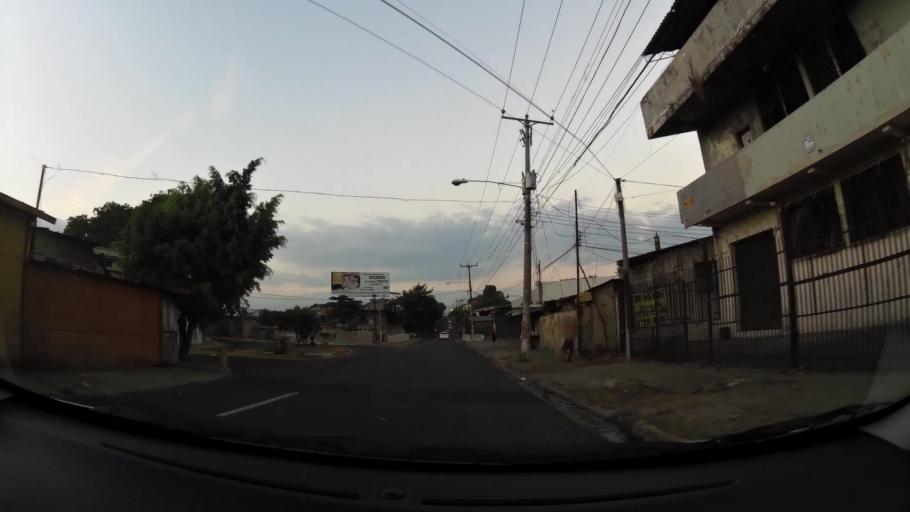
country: SV
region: San Salvador
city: San Salvador
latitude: 13.7053
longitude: -89.1863
